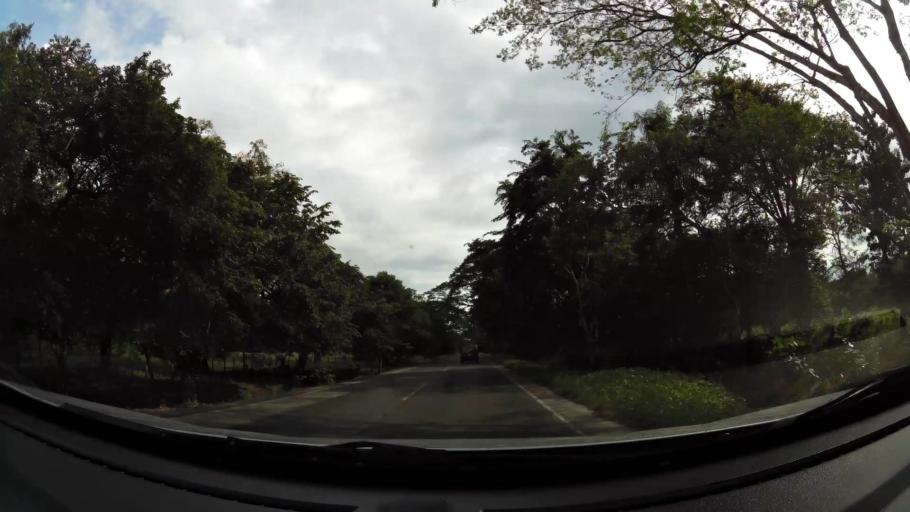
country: CR
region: Guanacaste
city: Juntas
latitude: 10.2287
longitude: -84.9791
